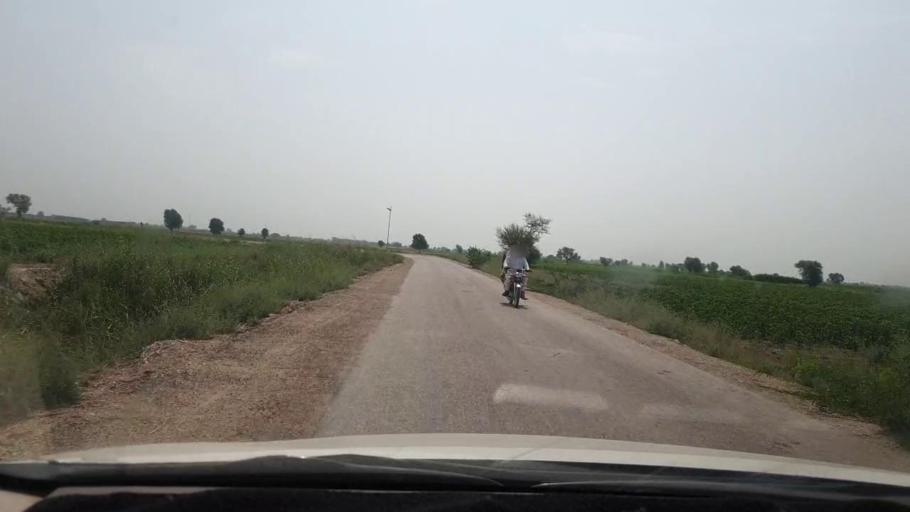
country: PK
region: Sindh
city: Rohri
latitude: 27.5376
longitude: 69.0028
